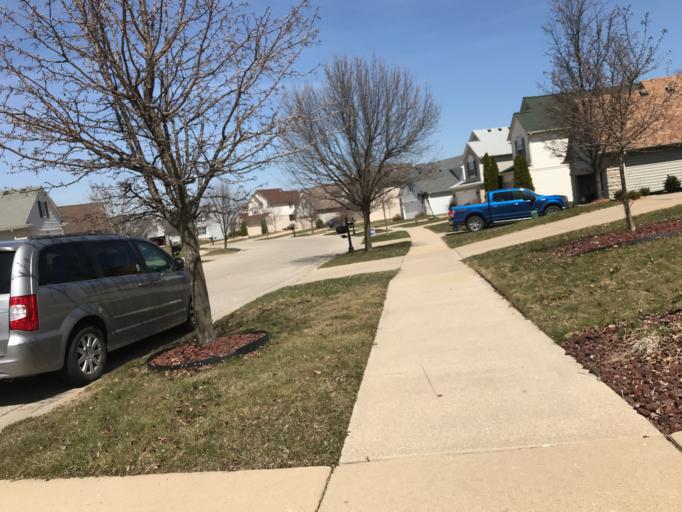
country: US
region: Michigan
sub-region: Washtenaw County
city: Ann Arbor
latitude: 42.2620
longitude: -83.7849
